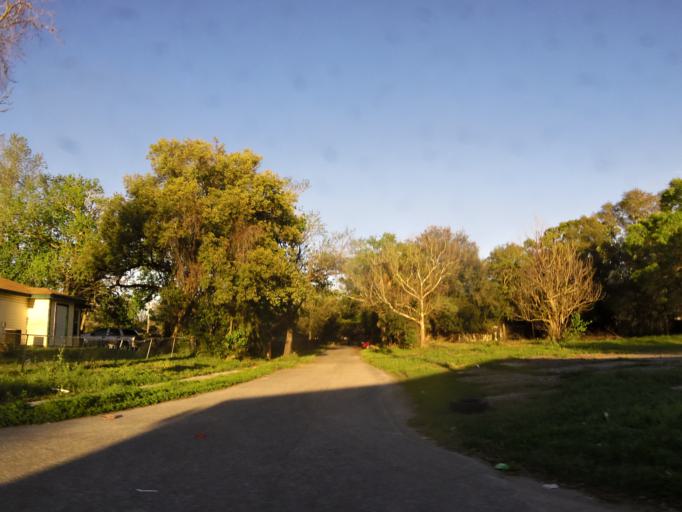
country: US
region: Florida
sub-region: Duval County
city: Jacksonville
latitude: 30.3348
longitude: -81.6984
